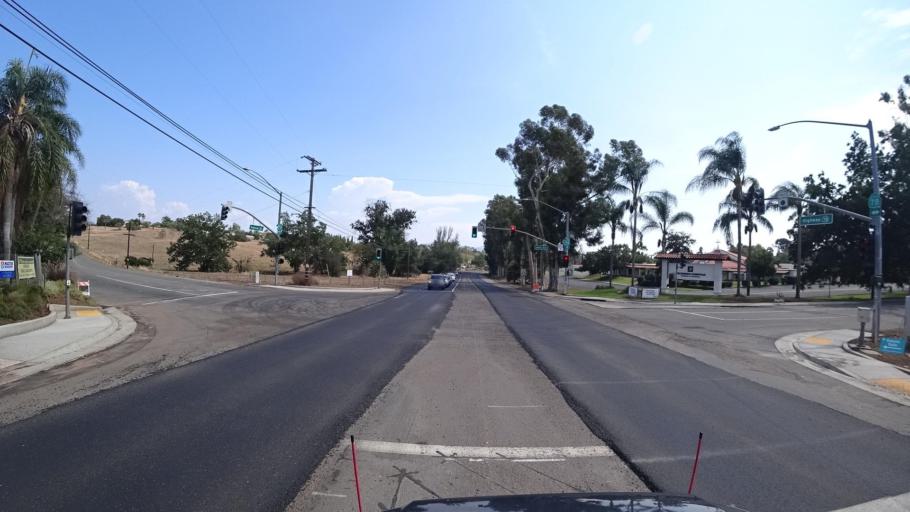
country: US
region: California
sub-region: San Diego County
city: Escondido
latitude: 33.1160
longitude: -117.0590
